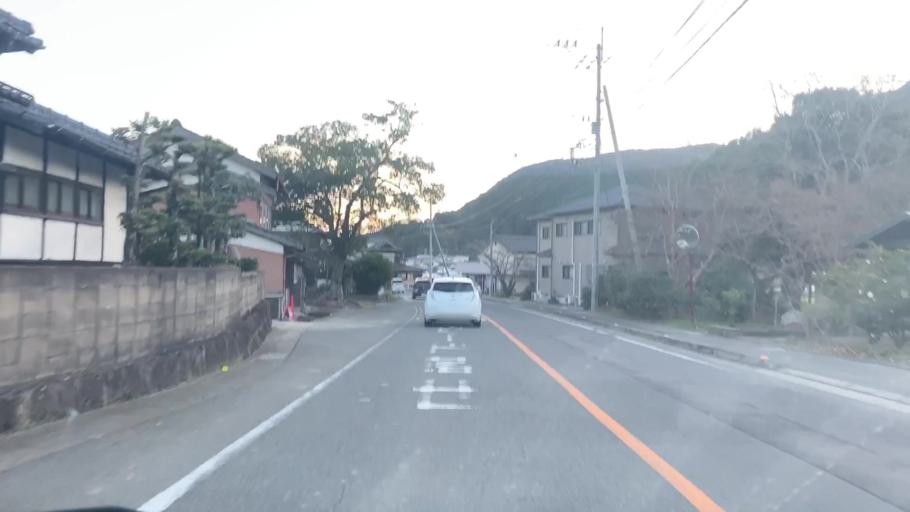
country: JP
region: Saga Prefecture
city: Takeocho-takeo
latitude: 33.2243
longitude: 130.0256
